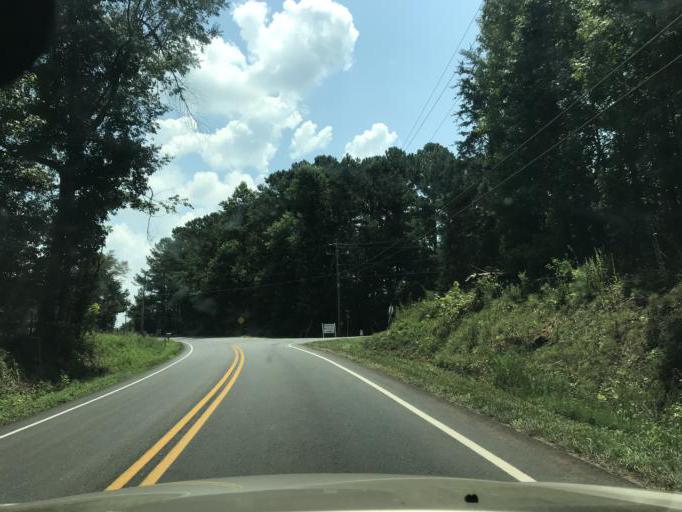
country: US
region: Georgia
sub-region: Dawson County
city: Dawsonville
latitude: 34.3355
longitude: -84.1486
